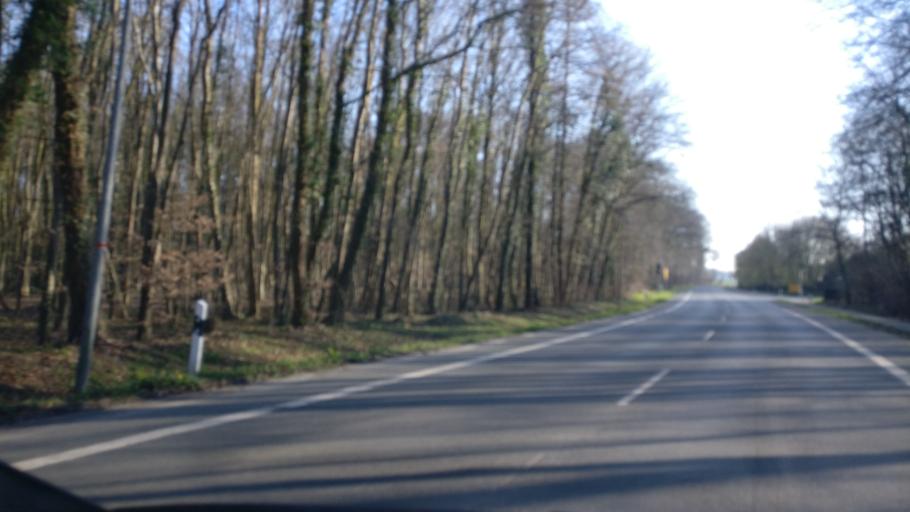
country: DE
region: North Rhine-Westphalia
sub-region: Regierungsbezirk Detmold
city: Lage
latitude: 52.0160
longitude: 8.7497
